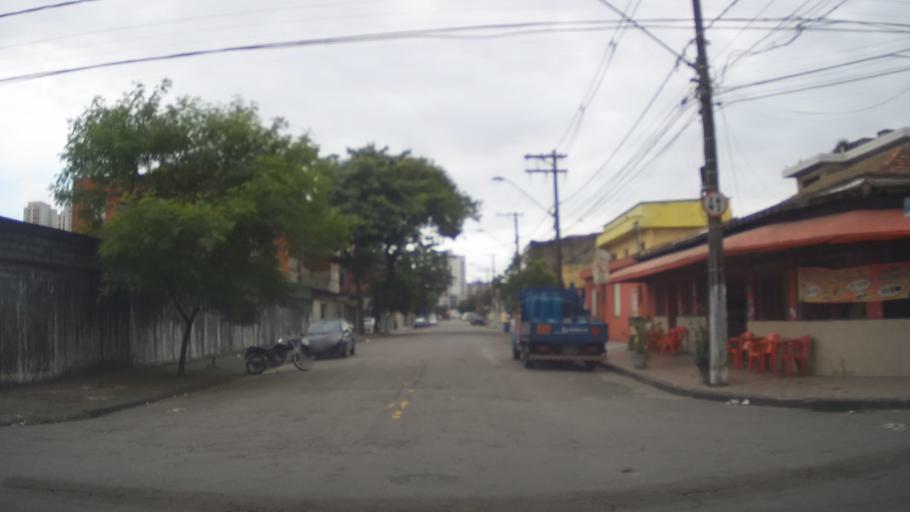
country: BR
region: Sao Paulo
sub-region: Santos
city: Santos
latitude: -23.9760
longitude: -46.2954
